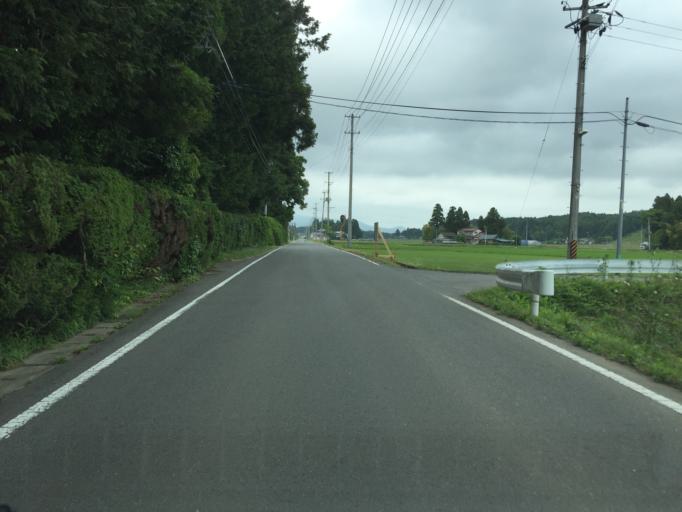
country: JP
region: Fukushima
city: Namie
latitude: 37.7267
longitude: 140.9358
